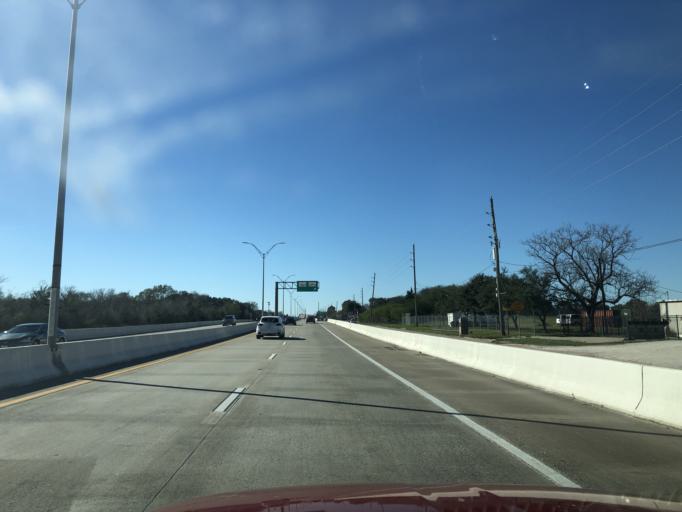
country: US
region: Texas
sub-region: Fort Bend County
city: Mission Bend
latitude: 29.7086
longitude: -95.6759
